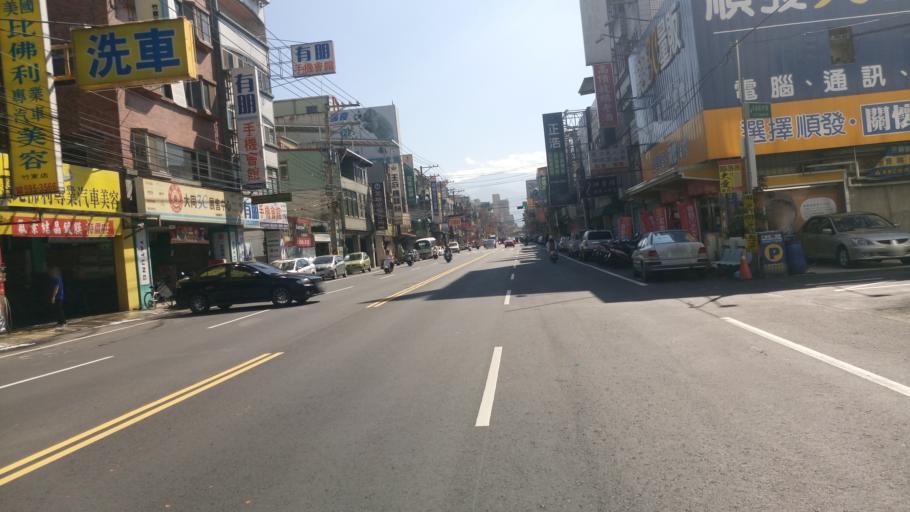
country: TW
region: Taiwan
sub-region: Hsinchu
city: Zhubei
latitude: 24.7467
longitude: 121.0808
